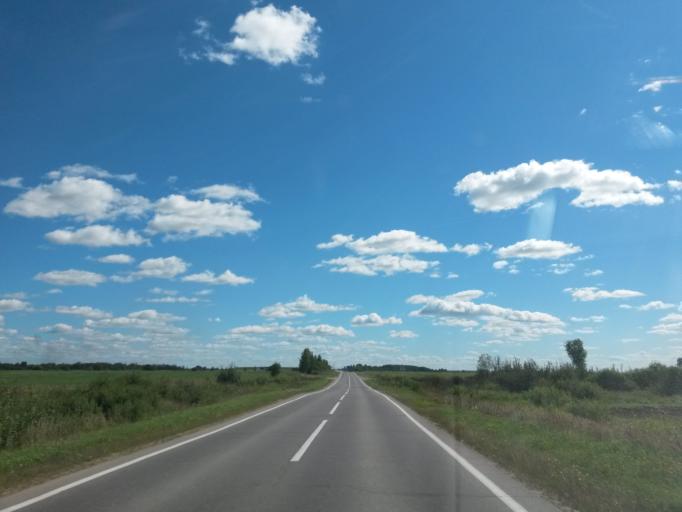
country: RU
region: Jaroslavl
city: Yaroslavl
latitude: 57.7488
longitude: 39.8798
